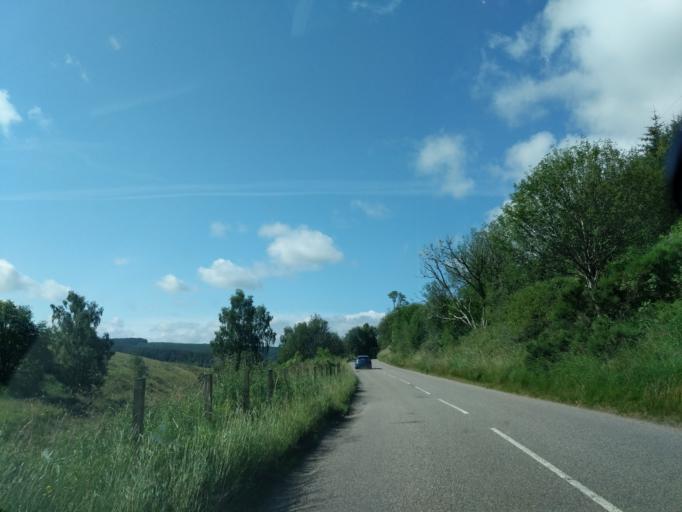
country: GB
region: Scotland
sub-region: Moray
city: Dufftown
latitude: 57.3718
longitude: -3.2524
